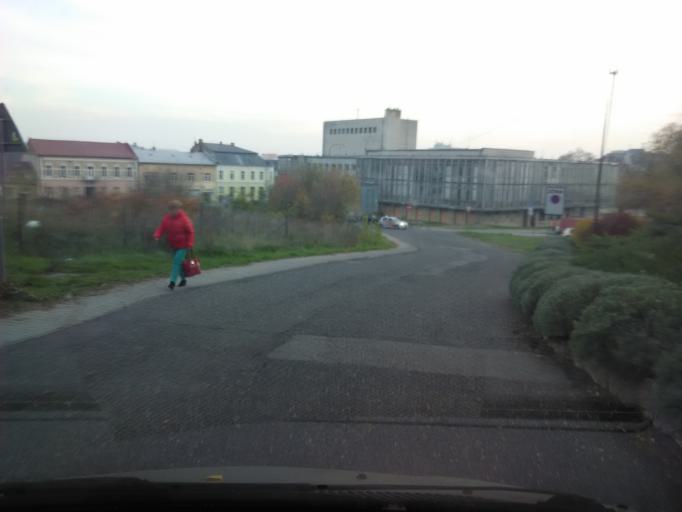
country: SK
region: Nitriansky
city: Levice
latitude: 48.2218
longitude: 18.6079
